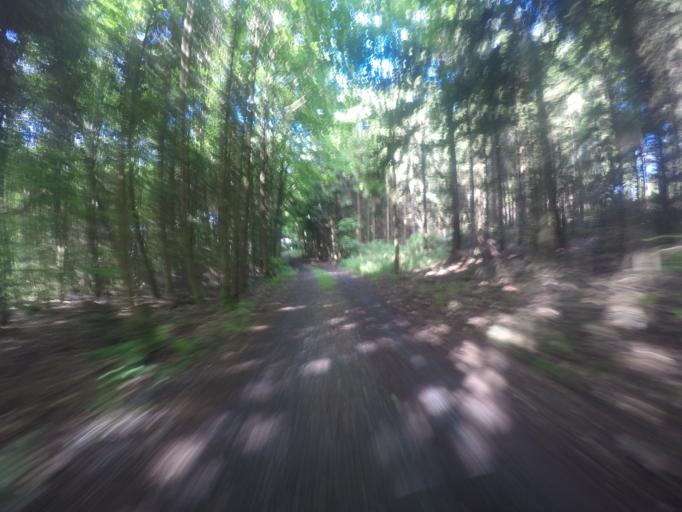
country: DE
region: Bavaria
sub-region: Upper Franconia
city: Schonwald
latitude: 50.1932
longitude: 12.0613
